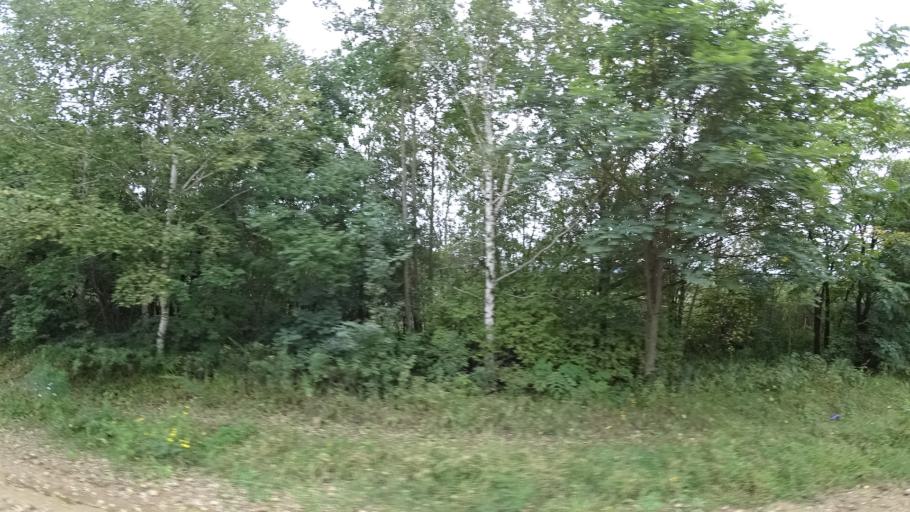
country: RU
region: Primorskiy
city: Rettikhovka
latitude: 44.1571
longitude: 132.6846
